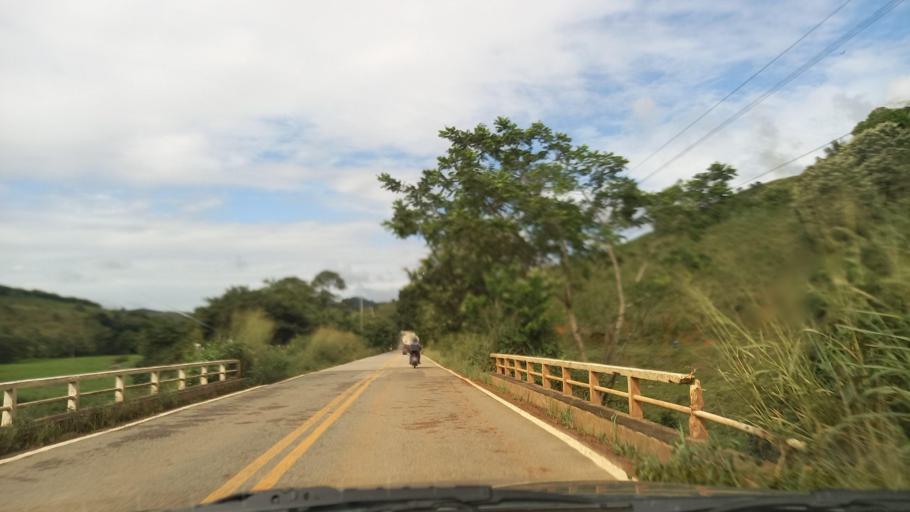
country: BR
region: Pernambuco
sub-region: Maraial
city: Maraial
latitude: -8.7502
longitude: -35.8273
